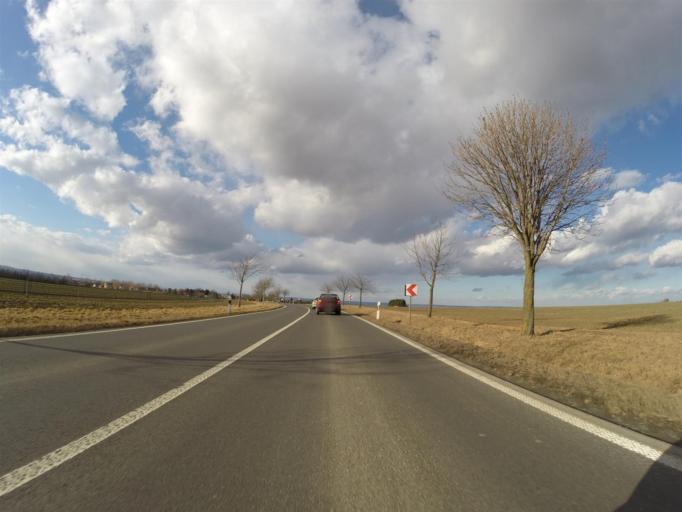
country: DE
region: Thuringia
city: Apolda
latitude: 50.9777
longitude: 11.5193
